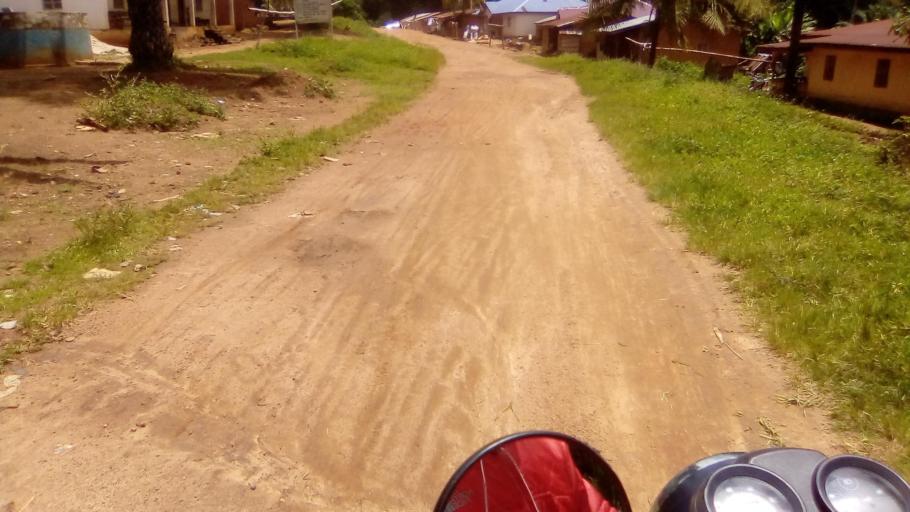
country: SL
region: Eastern Province
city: Giehun
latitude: 8.5070
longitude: -10.9047
